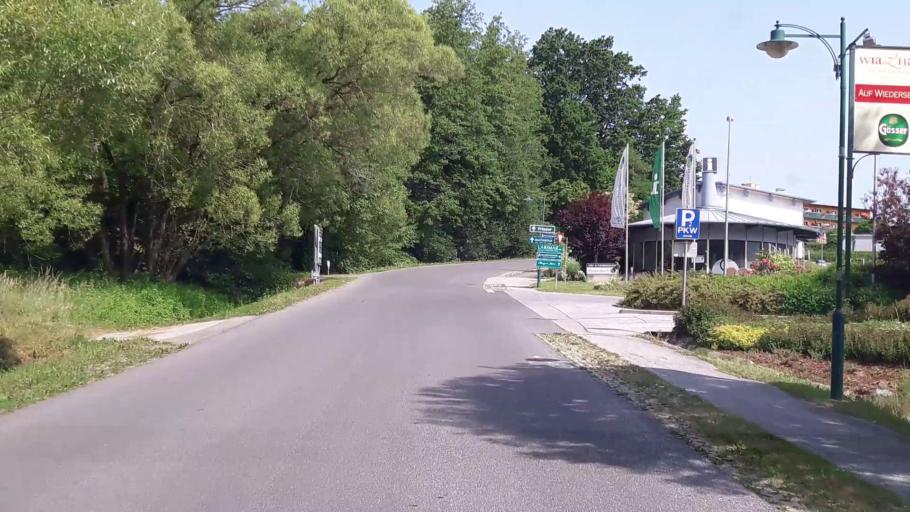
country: AT
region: Burgenland
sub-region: Politischer Bezirk Gussing
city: Stegersbach
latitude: 47.1694
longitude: 16.1490
